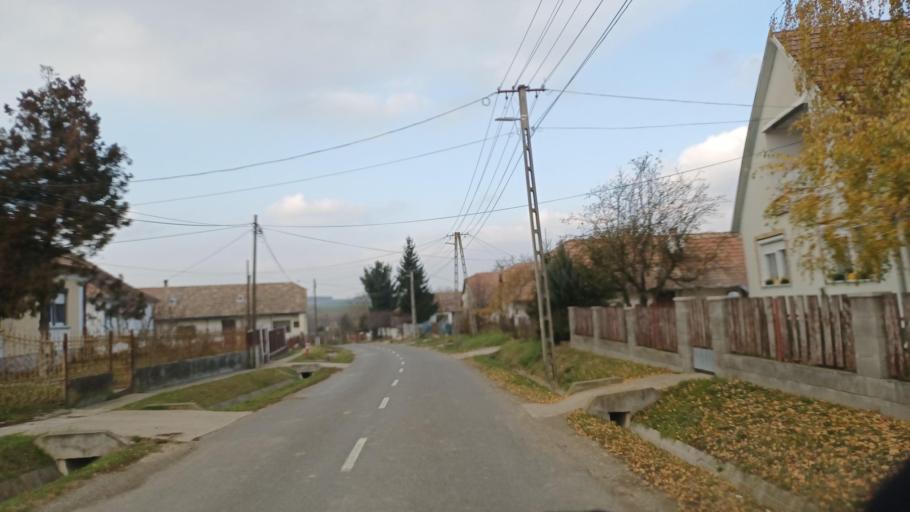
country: HU
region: Tolna
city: Gyonk
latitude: 46.5345
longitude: 18.4486
